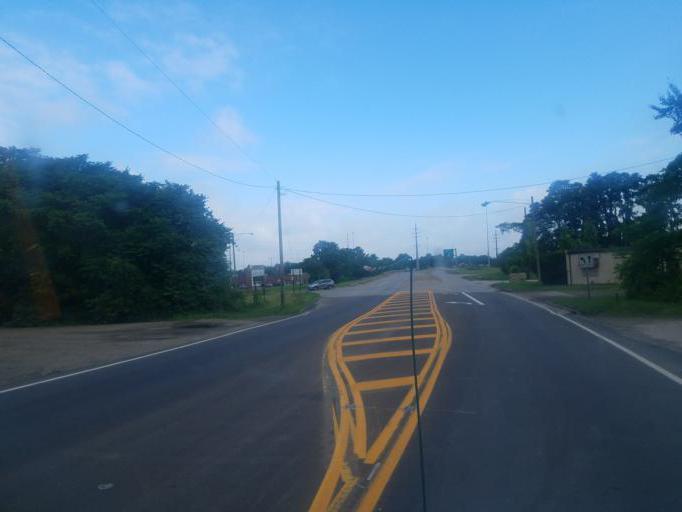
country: US
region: Ohio
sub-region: Stark County
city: Canton
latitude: 40.7850
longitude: -81.3474
